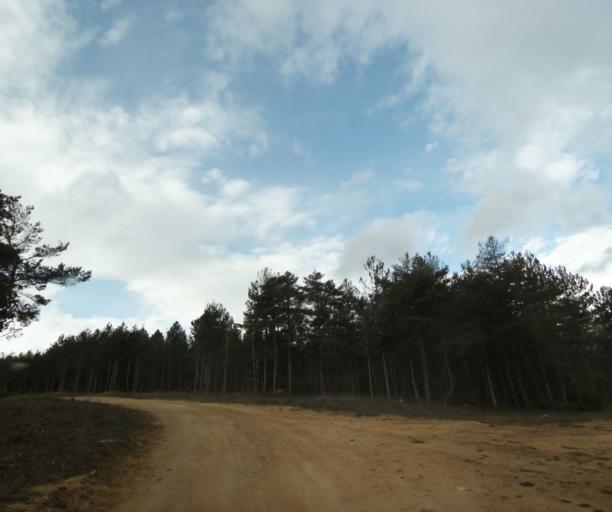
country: FR
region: Midi-Pyrenees
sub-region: Departement de l'Aveyron
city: Millau
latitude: 44.1281
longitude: 3.1528
